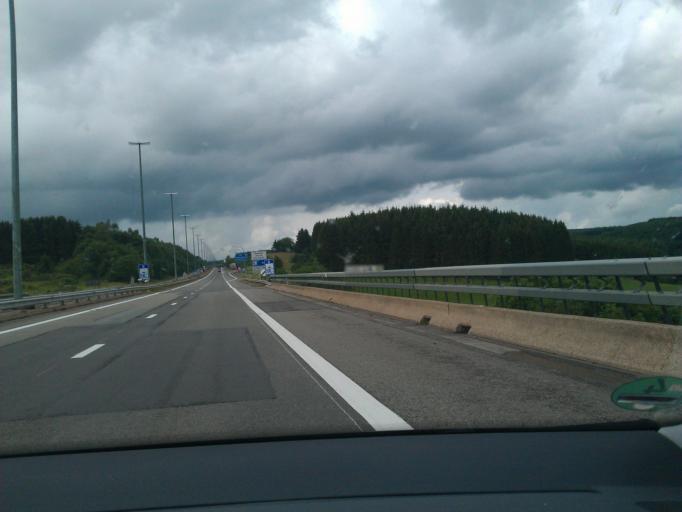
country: DE
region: Rheinland-Pfalz
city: Winterspelt
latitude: 50.2404
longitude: 6.1790
